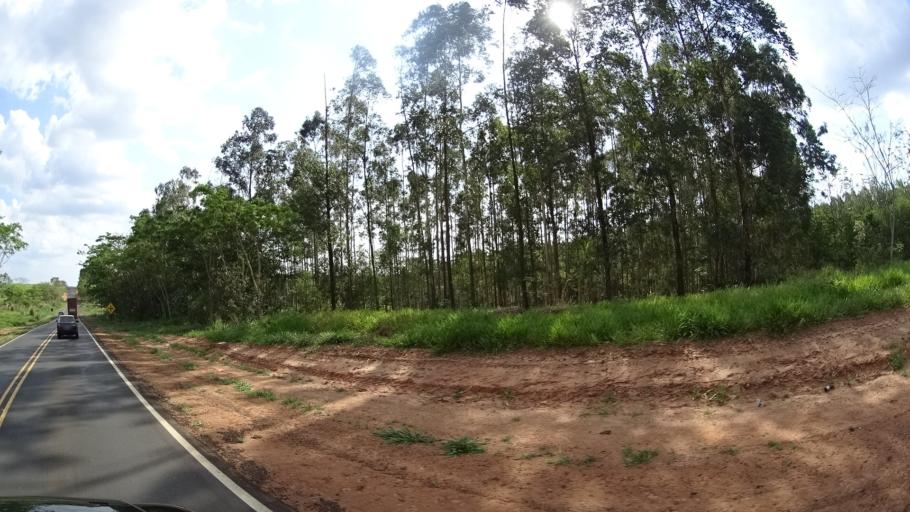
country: BR
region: Sao Paulo
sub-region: Urupes
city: Urupes
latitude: -21.1661
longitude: -49.2881
